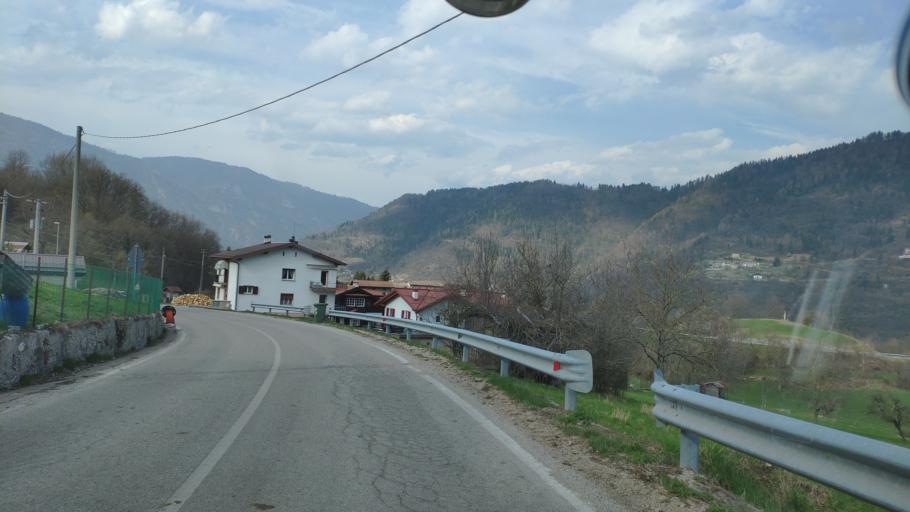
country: IT
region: Veneto
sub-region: Provincia di Vicenza
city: Enego
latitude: 45.9425
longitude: 11.7194
